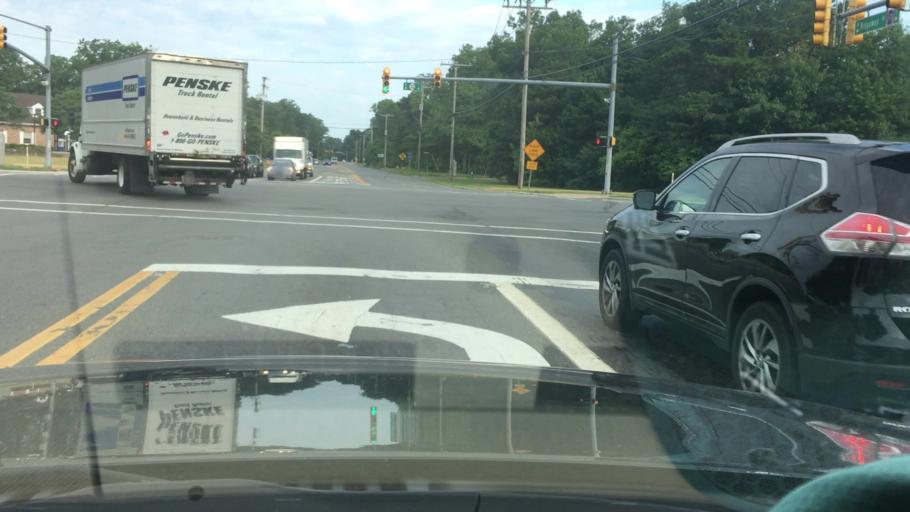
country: US
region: New Jersey
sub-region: Ocean County
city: Leisure Village West-Pine Lake Park
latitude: 40.0233
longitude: -74.2692
